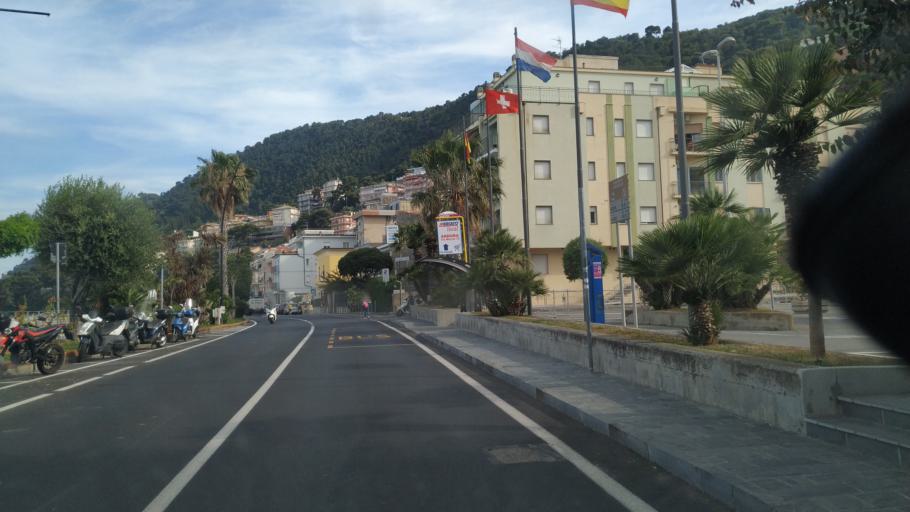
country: IT
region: Liguria
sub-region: Provincia di Savona
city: Laigueglia
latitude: 43.9726
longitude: 8.1598
